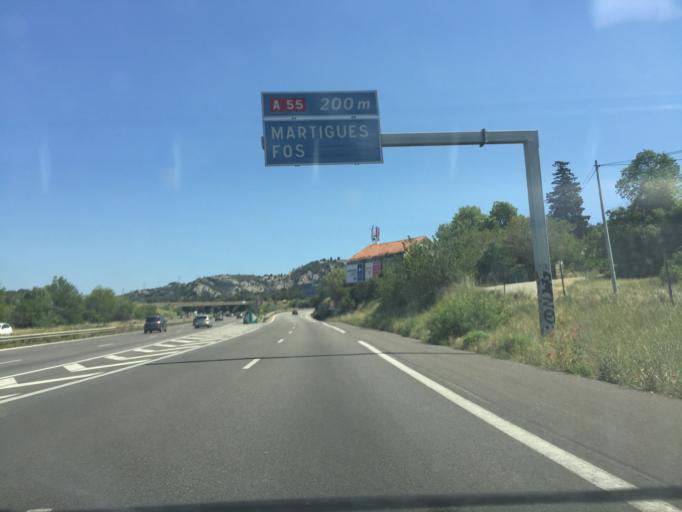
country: FR
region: Provence-Alpes-Cote d'Azur
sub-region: Departement des Bouches-du-Rhone
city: Les Pennes-Mirabeau
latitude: 43.4061
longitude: 5.2921
